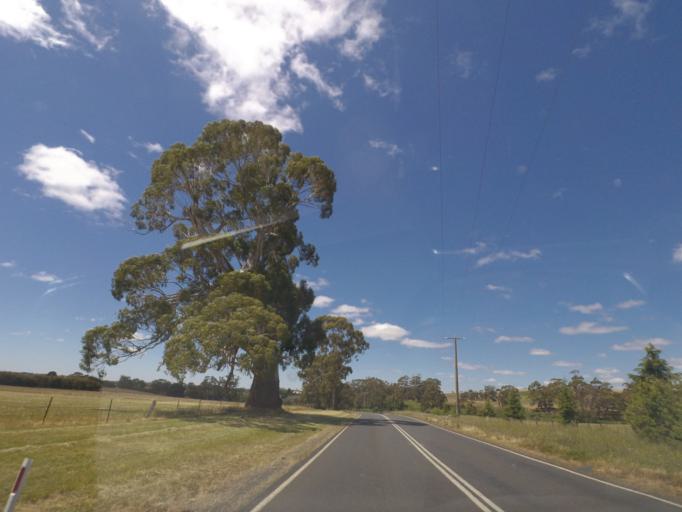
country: AU
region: Victoria
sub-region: Mount Alexander
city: Castlemaine
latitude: -37.3279
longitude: 144.1901
